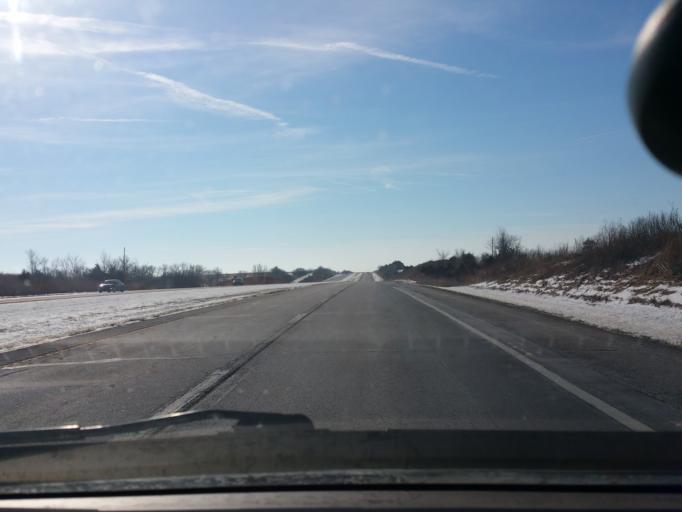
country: US
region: Missouri
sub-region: Harrison County
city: Bethany
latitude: 40.4420
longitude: -93.9842
